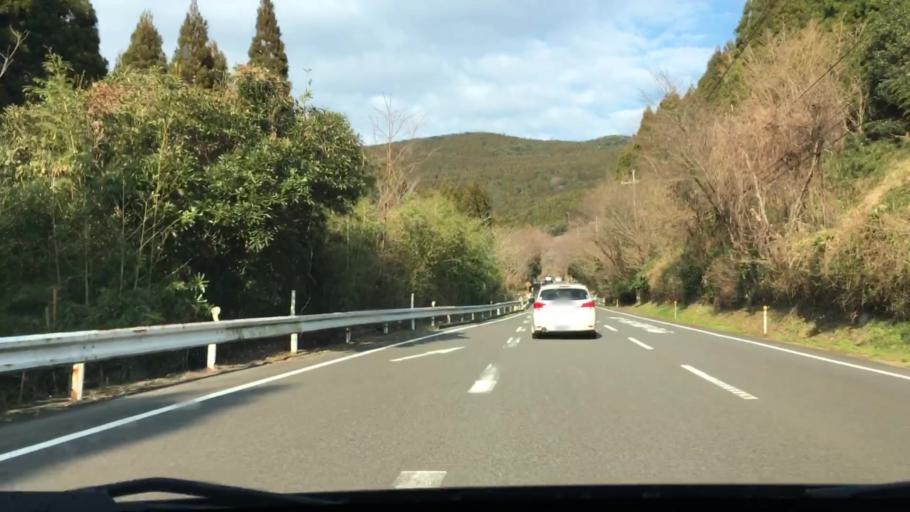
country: JP
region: Miyazaki
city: Miyazaki-shi
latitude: 31.7727
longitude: 131.3302
